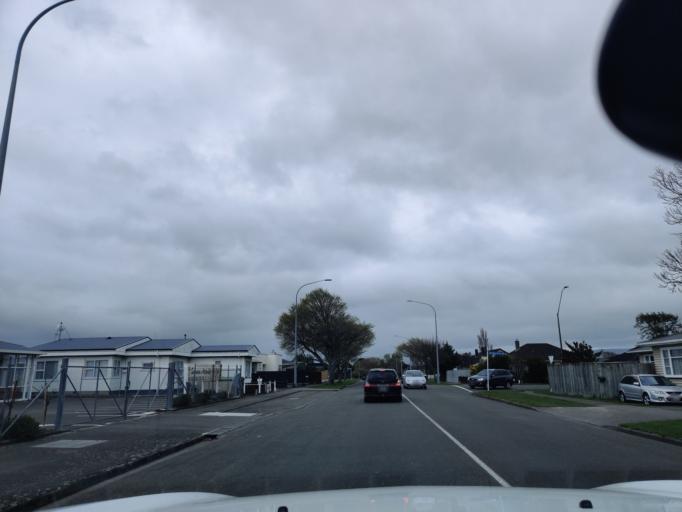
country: NZ
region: Manawatu-Wanganui
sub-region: Palmerston North City
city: Palmerston North
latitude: -40.3365
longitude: 175.6348
